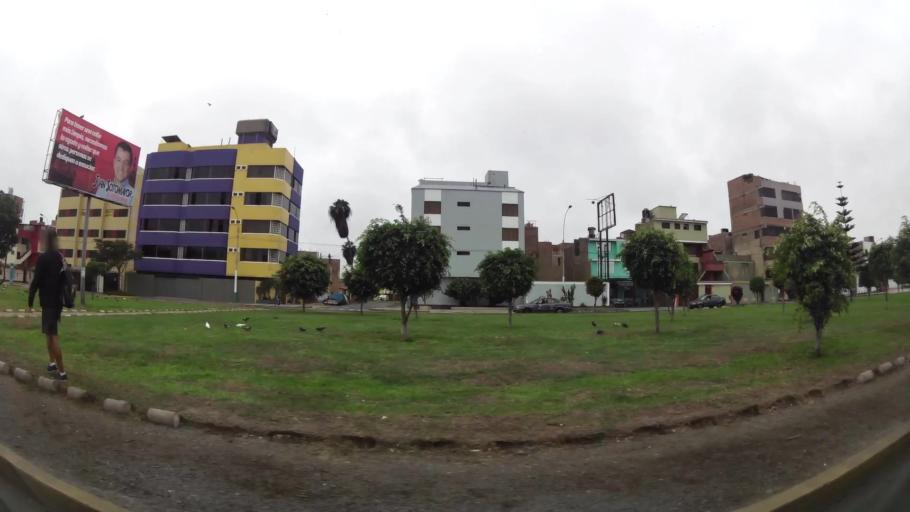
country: PE
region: Callao
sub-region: Callao
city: Callao
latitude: -12.0697
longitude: -77.1106
